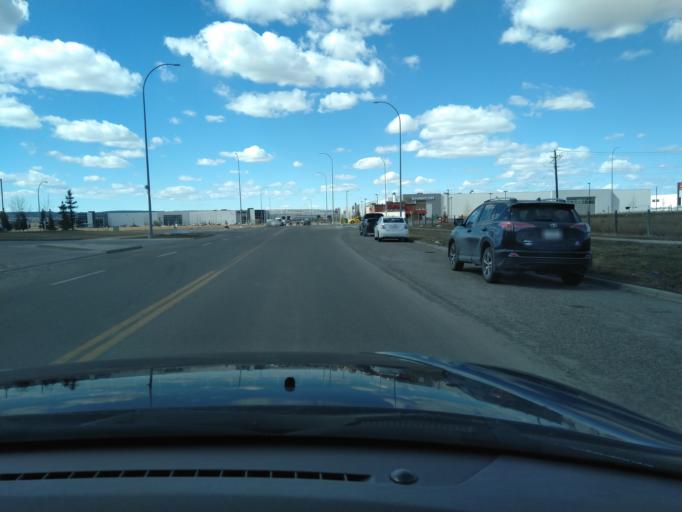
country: CA
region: Alberta
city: Calgary
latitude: 51.1434
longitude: -114.0117
